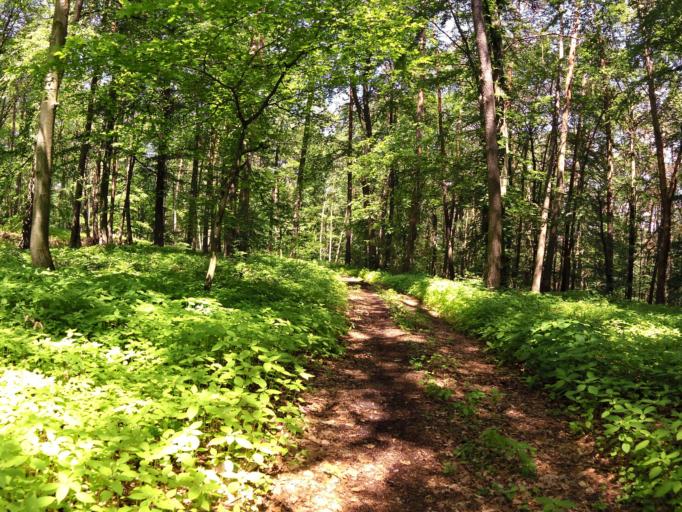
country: DE
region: Bavaria
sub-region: Regierungsbezirk Unterfranken
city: Eibelstadt
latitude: 49.7316
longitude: 10.0097
